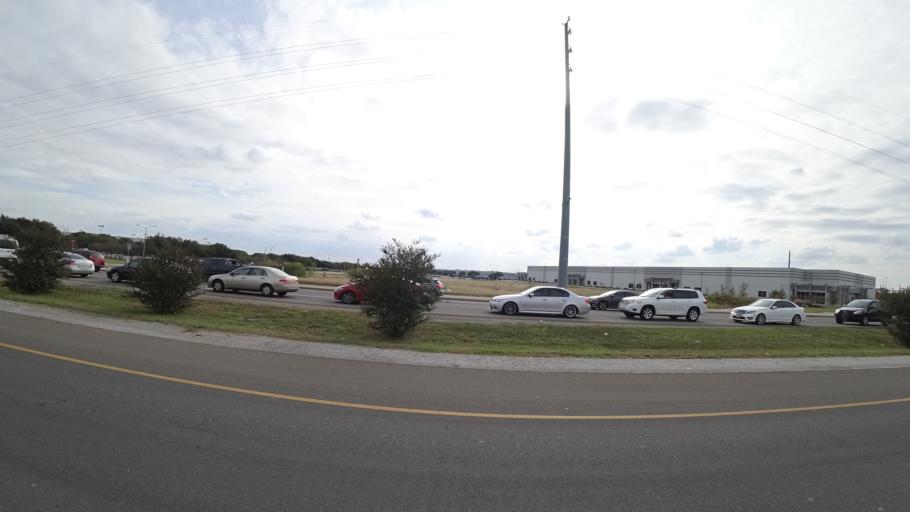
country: US
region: Texas
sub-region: Travis County
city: Wells Branch
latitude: 30.4198
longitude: -97.6615
